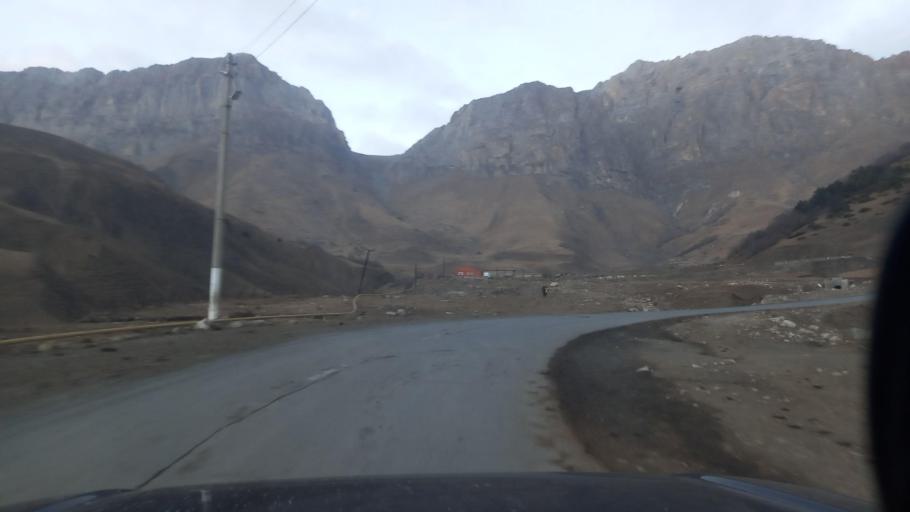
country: RU
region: Ingushetiya
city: Dzhayrakh
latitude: 42.8168
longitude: 44.8144
